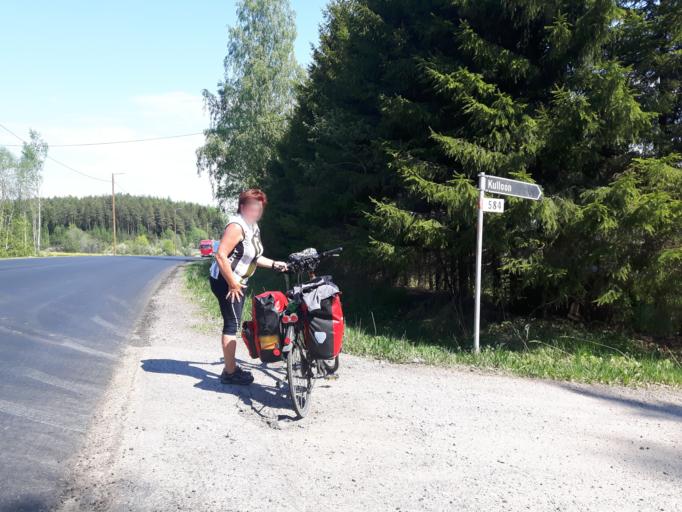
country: FI
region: Uusimaa
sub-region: Porvoo
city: Porvoo
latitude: 60.3637
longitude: 25.5443
